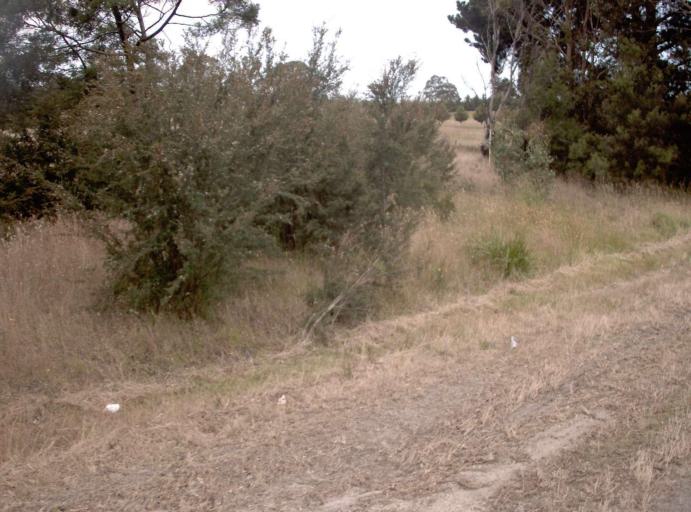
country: AU
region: Victoria
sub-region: Wellington
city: Sale
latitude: -38.2093
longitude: 147.1010
